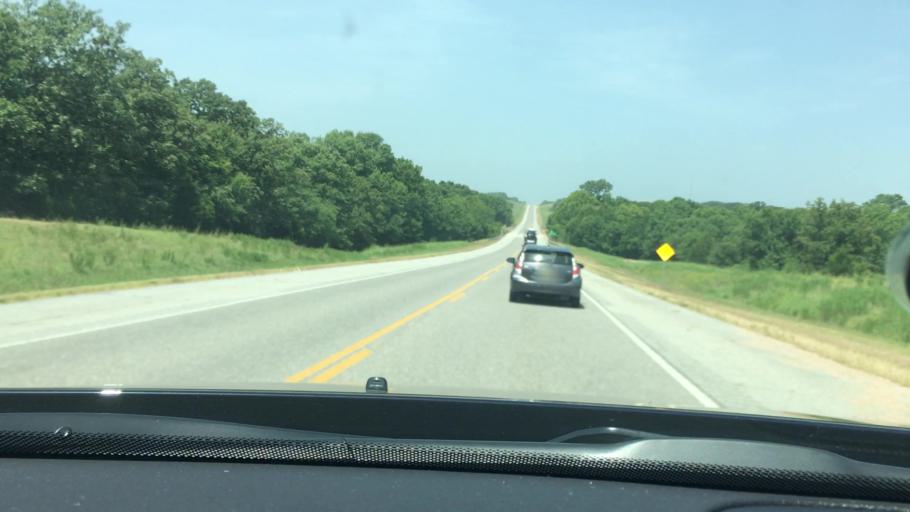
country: US
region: Oklahoma
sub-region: Coal County
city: Coalgate
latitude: 34.6110
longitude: -96.3902
